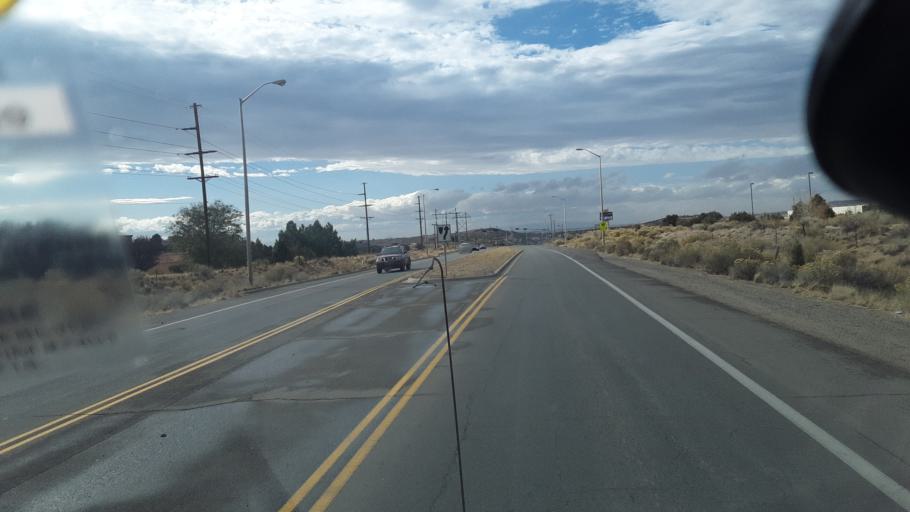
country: US
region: New Mexico
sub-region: San Juan County
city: Farmington
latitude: 36.7737
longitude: -108.1907
